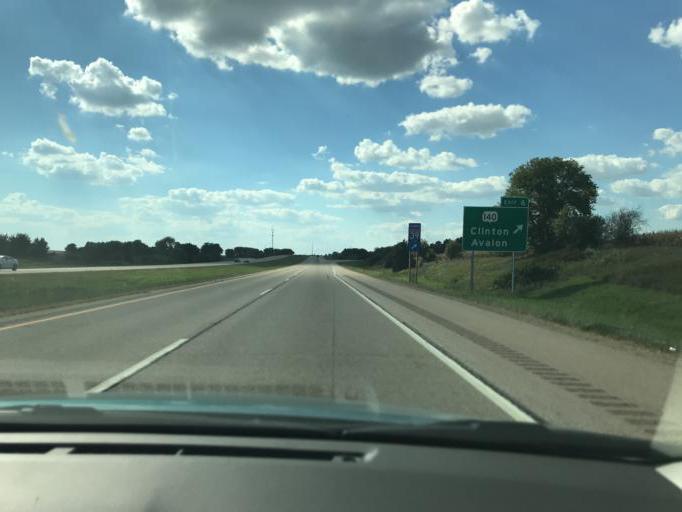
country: US
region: Wisconsin
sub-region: Rock County
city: Clinton
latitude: 42.5728
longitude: -88.8560
